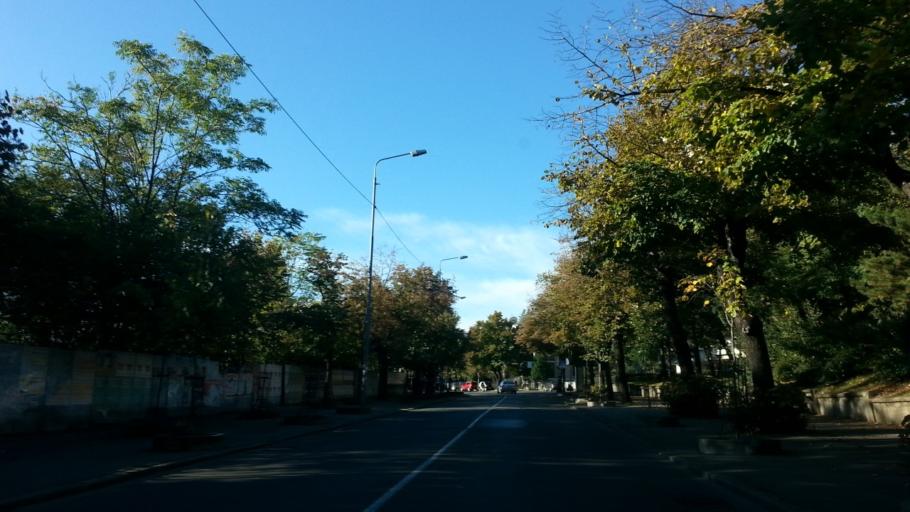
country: RS
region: Central Serbia
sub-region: Belgrade
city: Savski Venac
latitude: 44.7866
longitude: 20.4637
